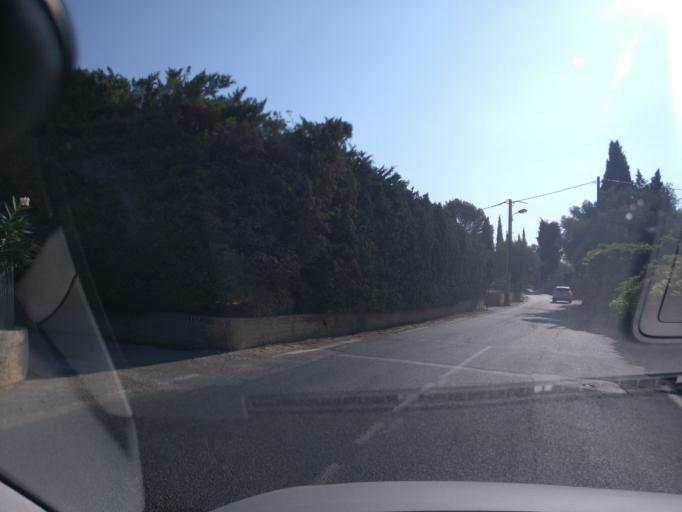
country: FR
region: Provence-Alpes-Cote d'Azur
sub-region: Departement du Var
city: Sanary-sur-Mer
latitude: 43.1380
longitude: 5.8124
